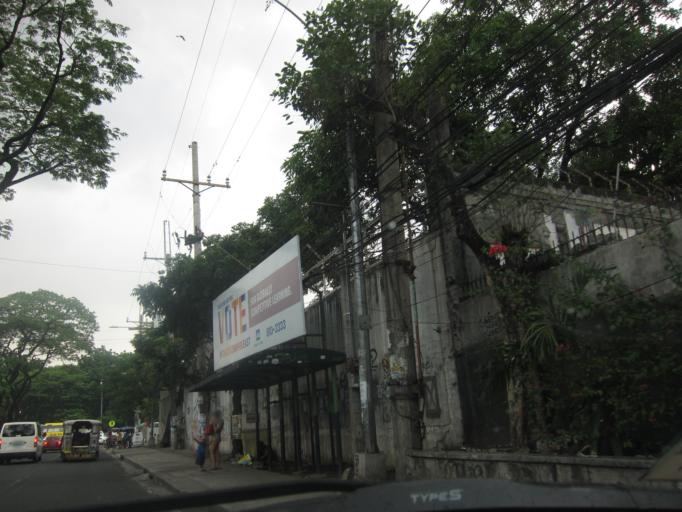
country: PH
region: Metro Manila
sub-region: Quezon City
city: Quezon City
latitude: 14.6481
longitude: 121.0516
